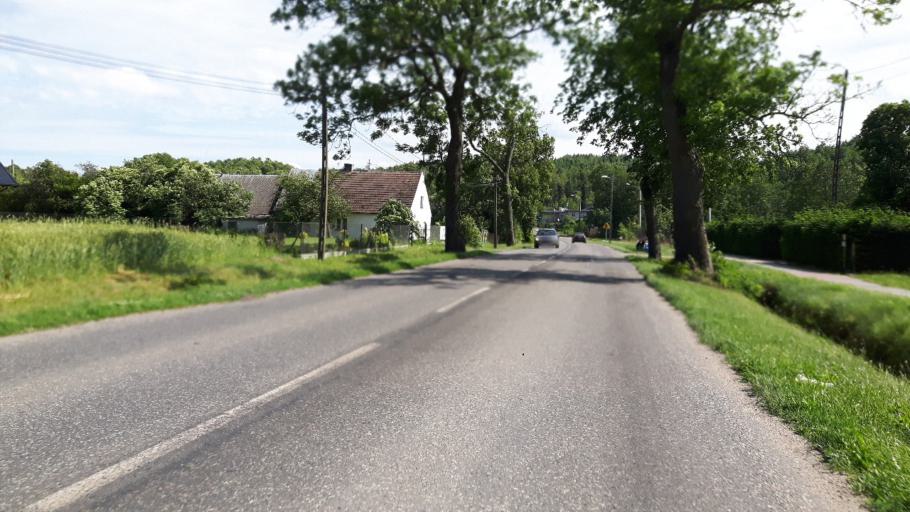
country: PL
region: Pomeranian Voivodeship
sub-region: Powiat wejherowski
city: Orle
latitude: 54.6516
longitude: 18.1007
